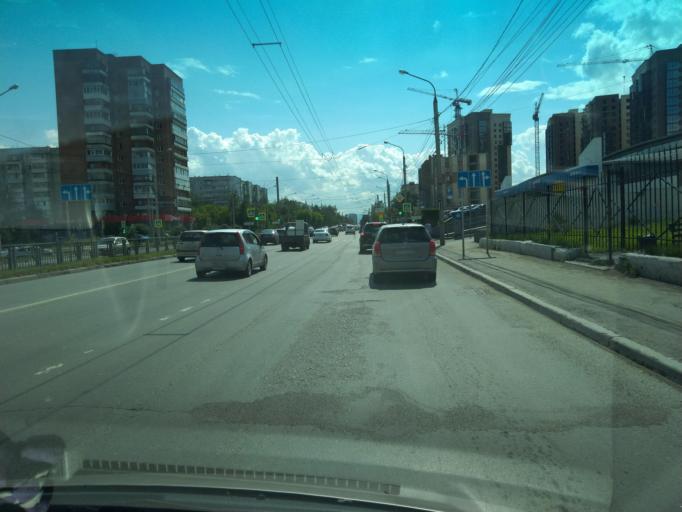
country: RU
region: Krasnoyarskiy
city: Solnechnyy
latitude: 56.0552
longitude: 92.9412
